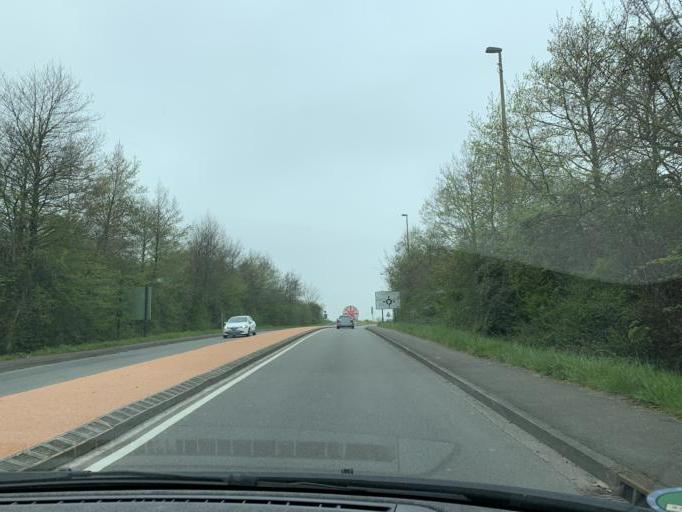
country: FR
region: Nord-Pas-de-Calais
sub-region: Departement du Pas-de-Calais
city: Coquelles
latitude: 50.9282
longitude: 1.8001
